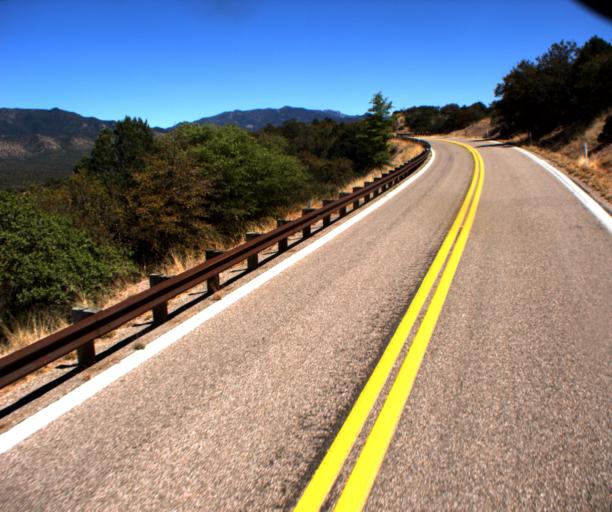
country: US
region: Arizona
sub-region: Cochise County
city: Sierra Vista
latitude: 31.4748
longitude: -110.4743
